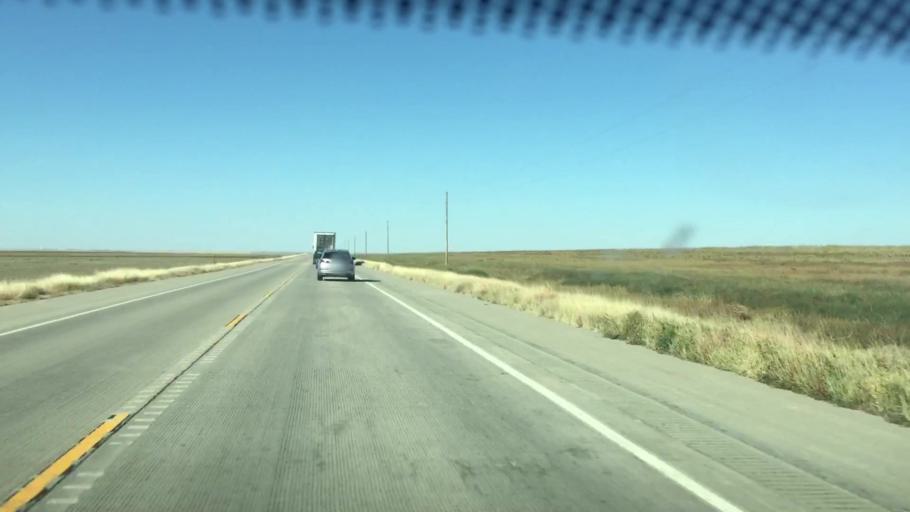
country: US
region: Colorado
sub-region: Kiowa County
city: Eads
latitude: 38.3068
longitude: -102.7199
